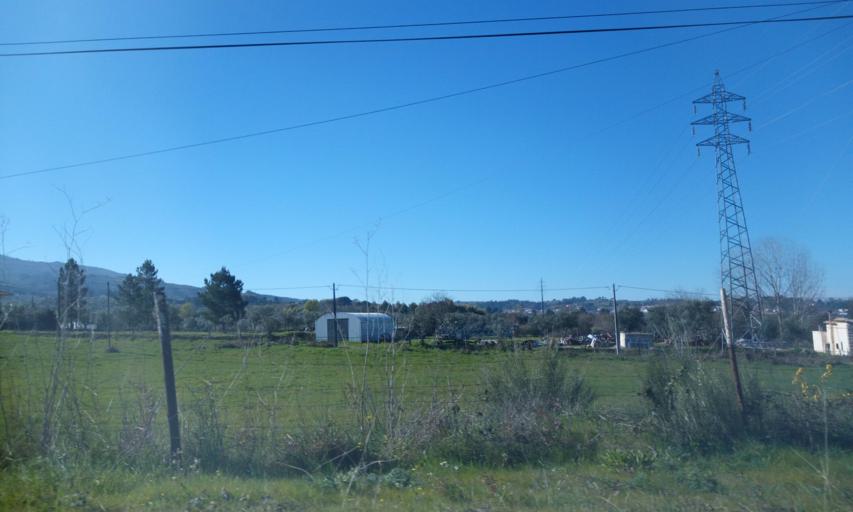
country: PT
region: Guarda
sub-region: Fornos de Algodres
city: Fornos de Algodres
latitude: 40.5304
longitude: -7.5595
